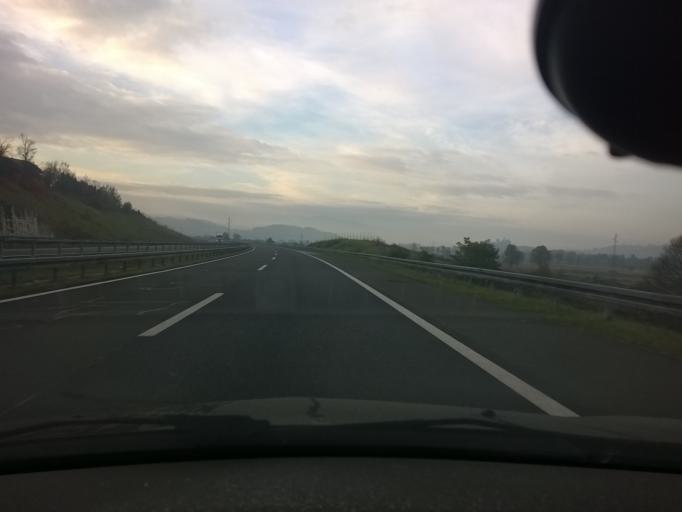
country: HR
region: Krapinsko-Zagorska
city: Zabok
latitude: 46.0551
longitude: 15.9191
